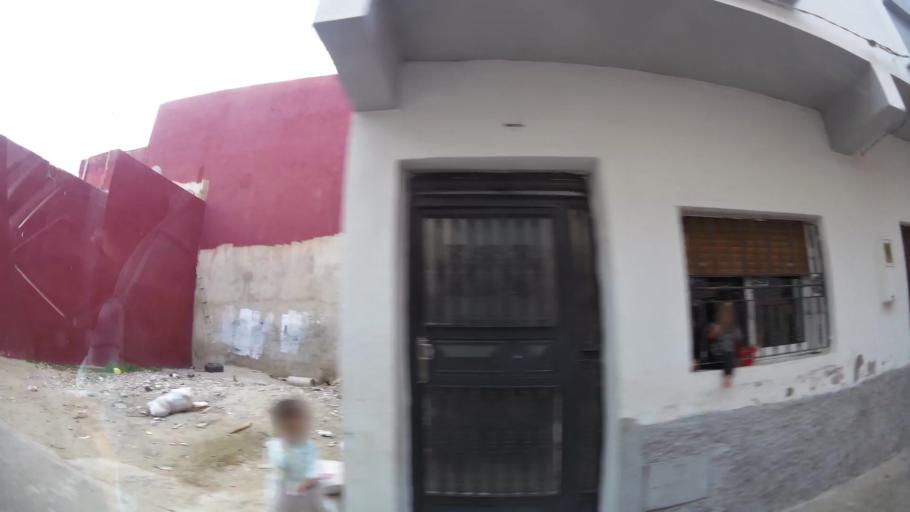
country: MA
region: Oriental
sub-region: Nador
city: Nador
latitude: 35.1593
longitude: -2.9117
